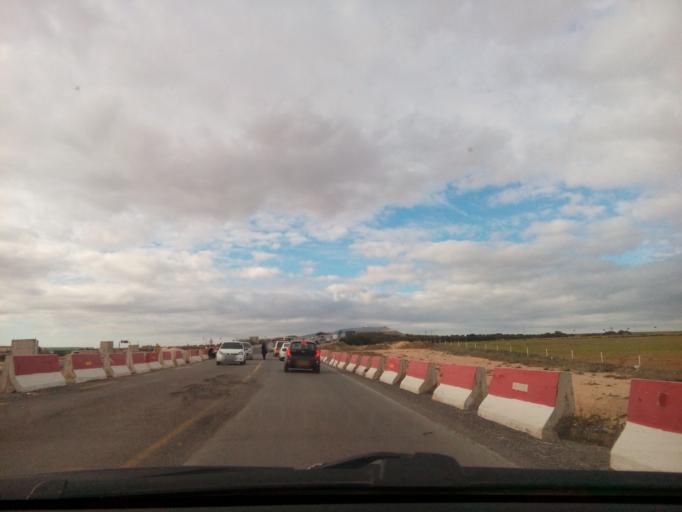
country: DZ
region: Sidi Bel Abbes
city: Sidi Bel Abbes
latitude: 35.2169
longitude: -0.6701
